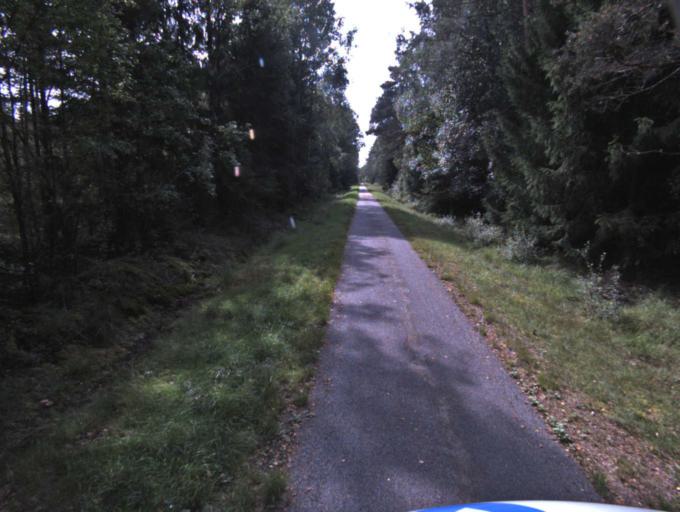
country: SE
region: Vaestra Goetaland
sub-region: Tranemo Kommun
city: Limmared
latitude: 57.6182
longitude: 13.3443
